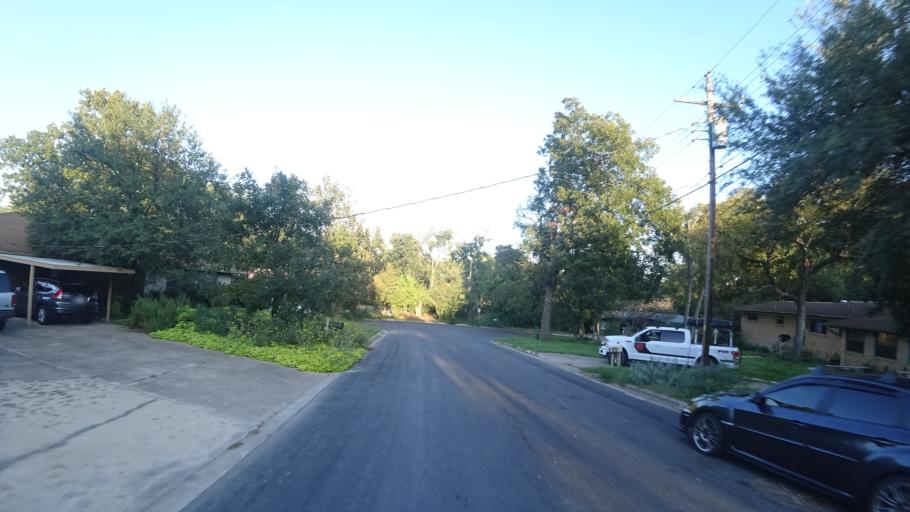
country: US
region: Texas
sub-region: Travis County
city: Wells Branch
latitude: 30.3664
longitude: -97.6730
